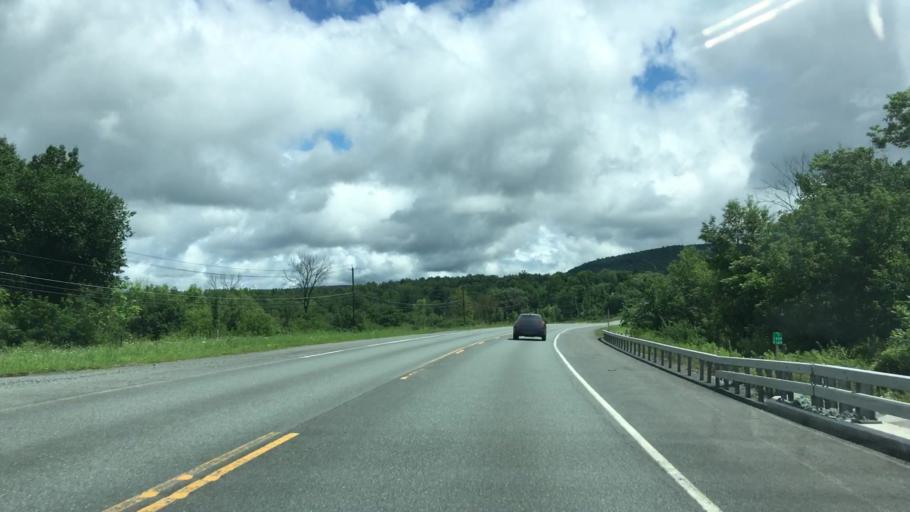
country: US
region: New York
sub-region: Rensselaer County
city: Hoosick Falls
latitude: 42.8464
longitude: -73.4656
